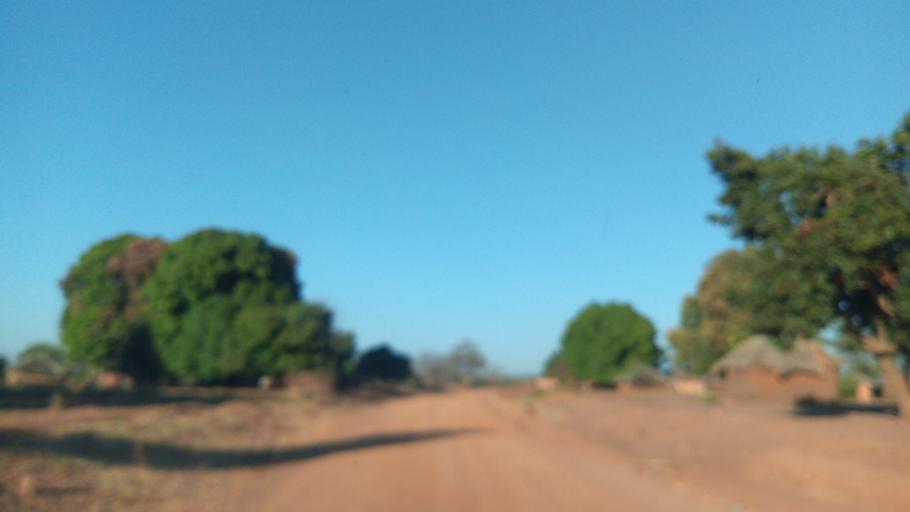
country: ZM
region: Luapula
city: Mwense
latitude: -10.4050
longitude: 28.6169
